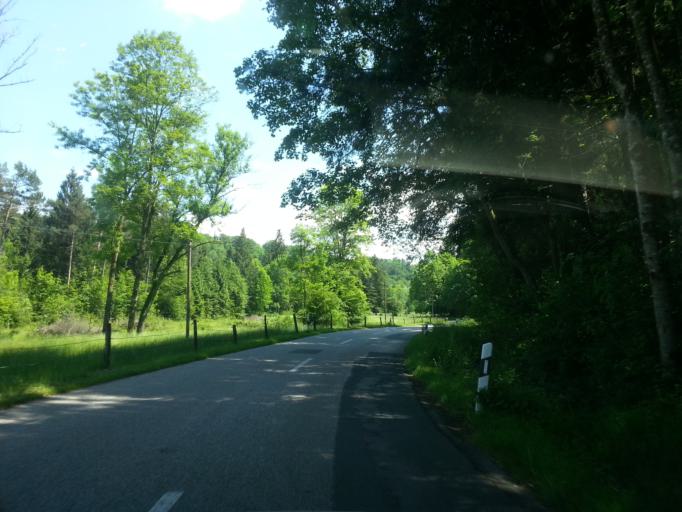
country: DE
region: Bavaria
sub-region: Upper Bavaria
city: Irschenberg
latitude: 47.8301
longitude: 11.8809
